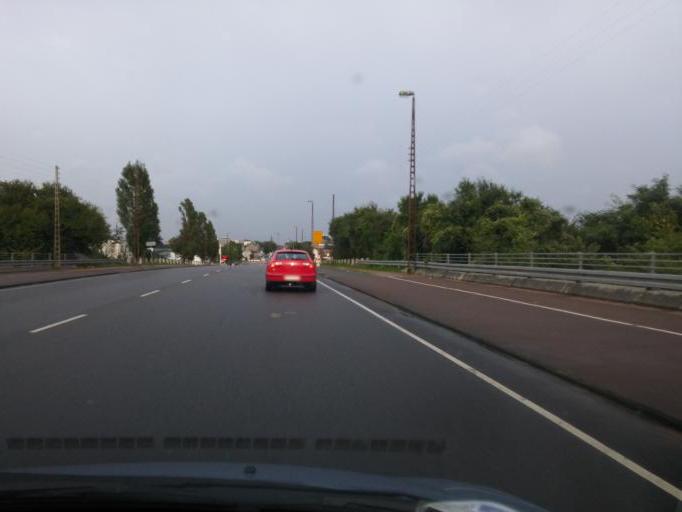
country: DK
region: South Denmark
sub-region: Odense Kommune
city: Odense
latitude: 55.3942
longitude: 10.3600
